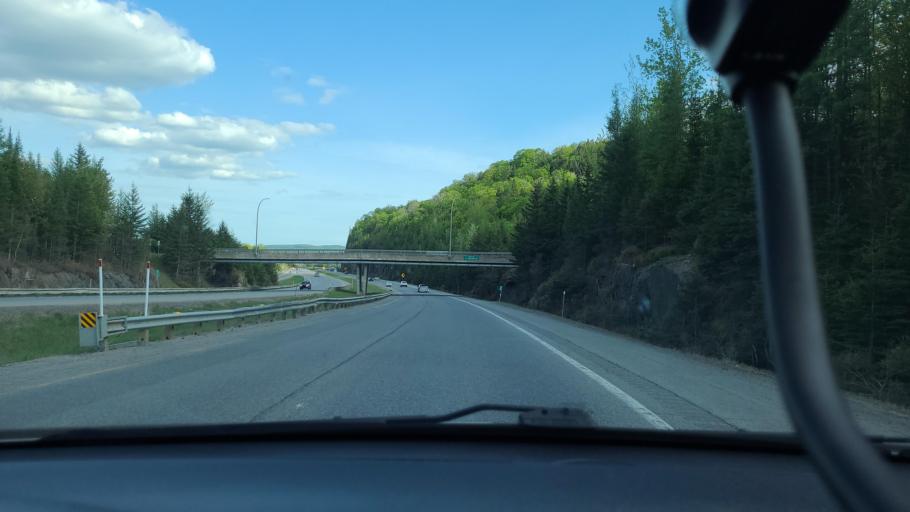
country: CA
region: Quebec
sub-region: Laurentides
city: Sainte-Adele
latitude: 45.9757
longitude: -74.1597
